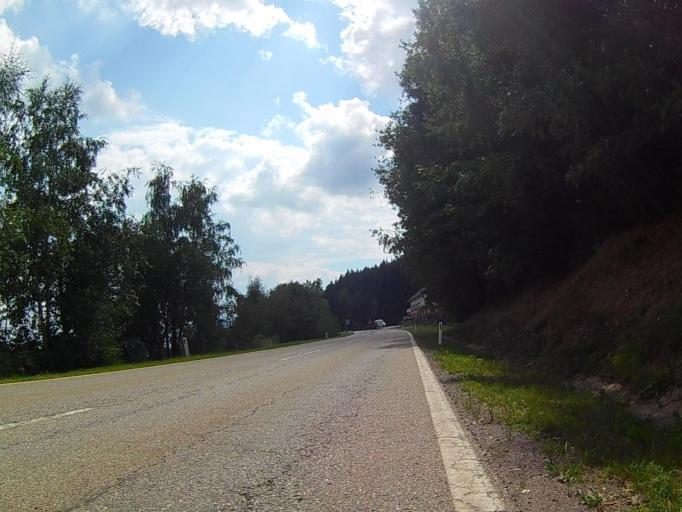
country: AT
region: Styria
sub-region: Politischer Bezirk Deutschlandsberg
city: Soboth
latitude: 46.6868
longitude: 15.1006
